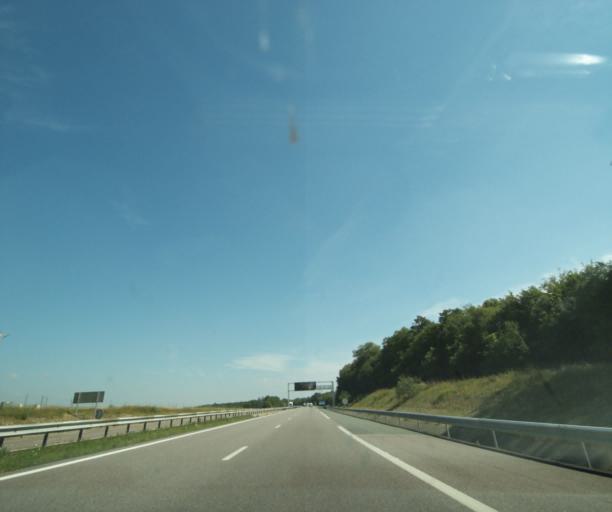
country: FR
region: Lorraine
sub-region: Departement de Meurthe-et-Moselle
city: Colombey-les-Belles
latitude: 48.5131
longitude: 5.9142
